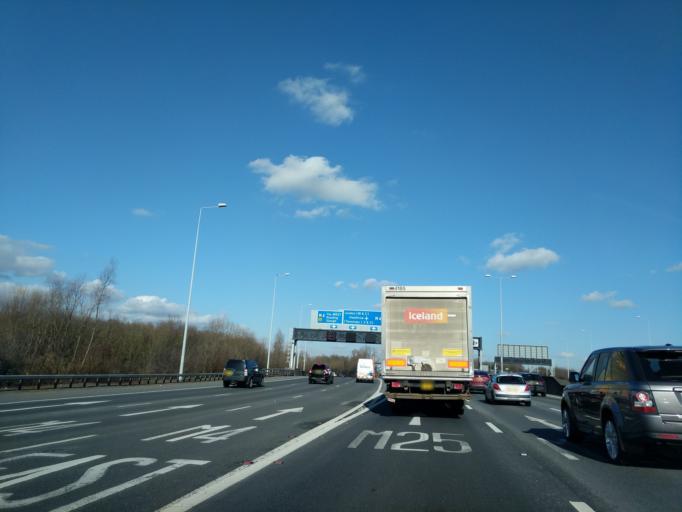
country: GB
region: England
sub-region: Buckinghamshire
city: Iver
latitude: 51.4890
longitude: -0.4960
